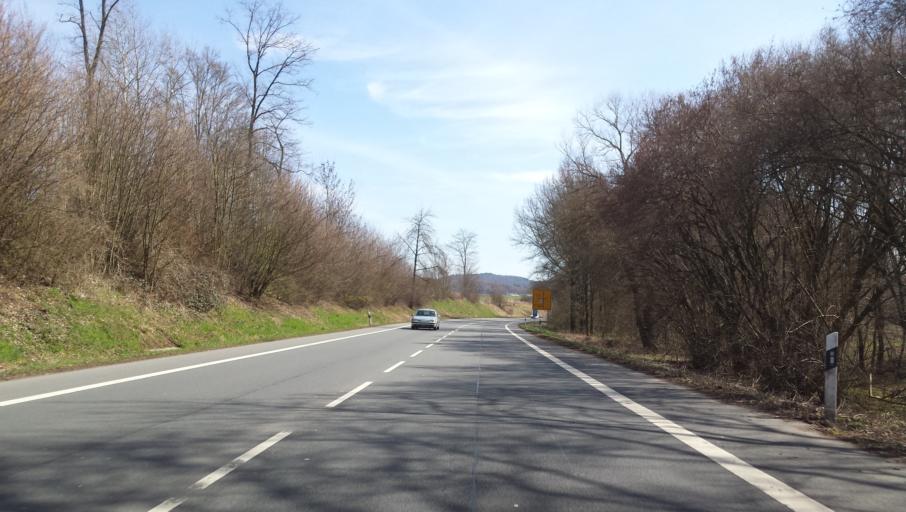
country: DE
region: Hesse
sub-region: Regierungsbezirk Darmstadt
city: Brensbach
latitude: 49.7877
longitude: 8.8589
